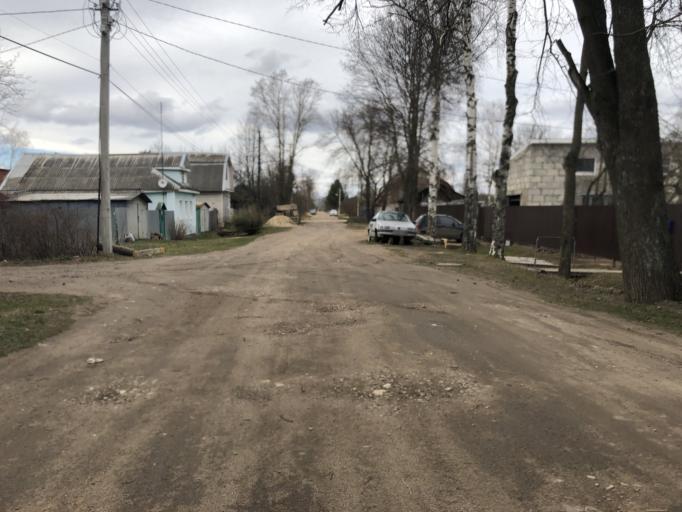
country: RU
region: Tverskaya
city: Rzhev
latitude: 56.2494
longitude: 34.3168
